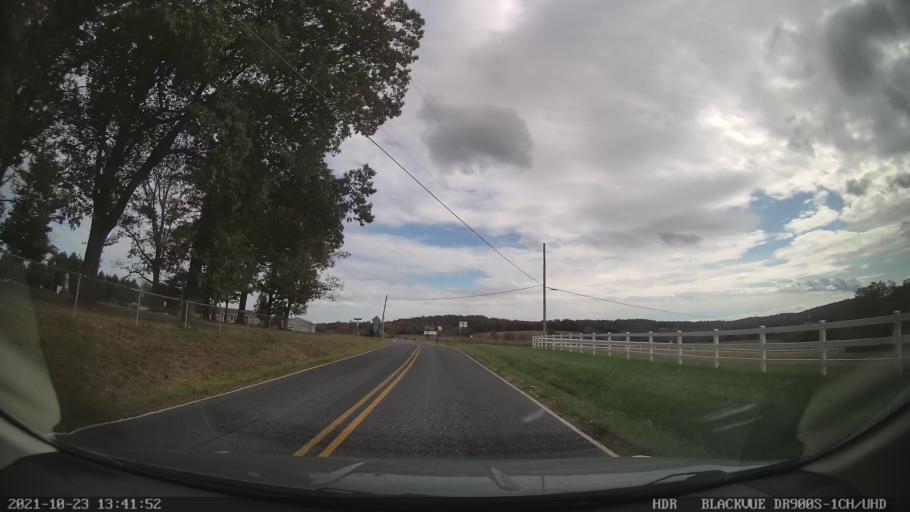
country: US
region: Pennsylvania
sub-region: Berks County
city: Bally
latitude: 40.4101
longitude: -75.5604
